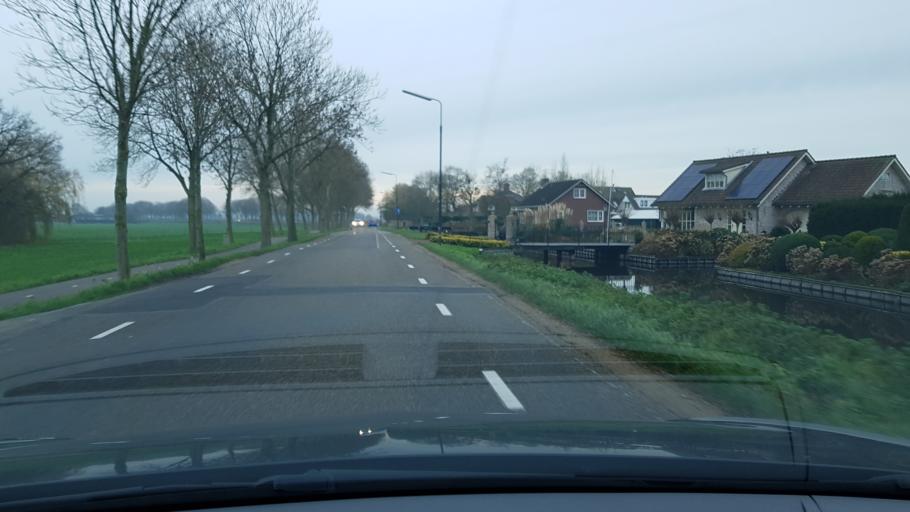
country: NL
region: North Holland
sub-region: Gemeente Uithoorn
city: Uithoorn
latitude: 52.2267
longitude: 4.8325
